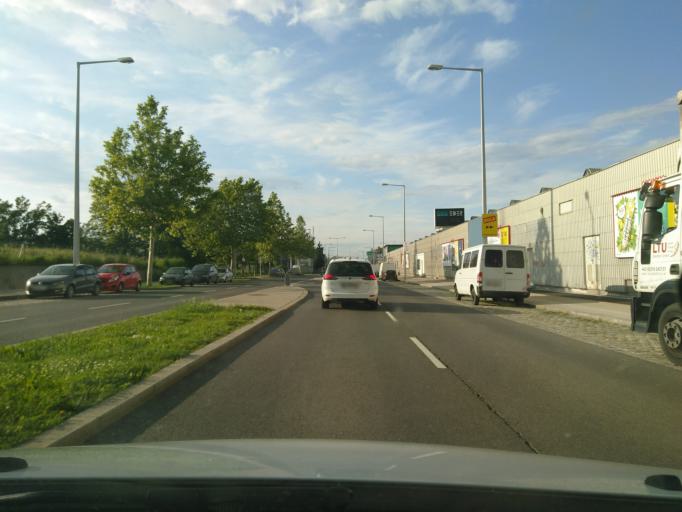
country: AT
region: Lower Austria
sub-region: Politischer Bezirk Modling
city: Brunn am Gebirge
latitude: 48.1356
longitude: 16.2981
